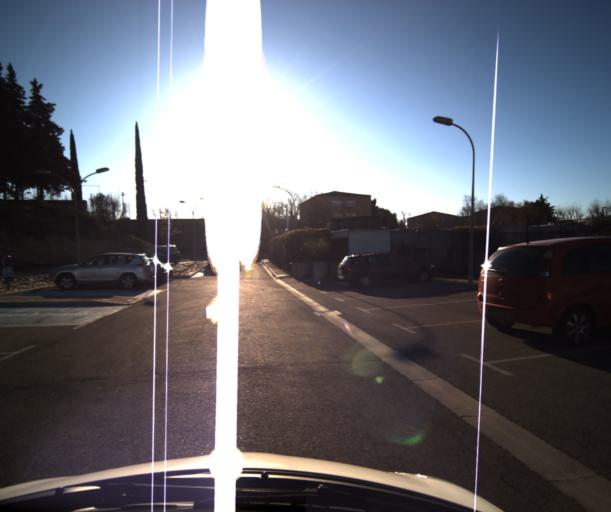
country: FR
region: Provence-Alpes-Cote d'Azur
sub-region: Departement du Vaucluse
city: Pertuis
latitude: 43.6962
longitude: 5.5090
